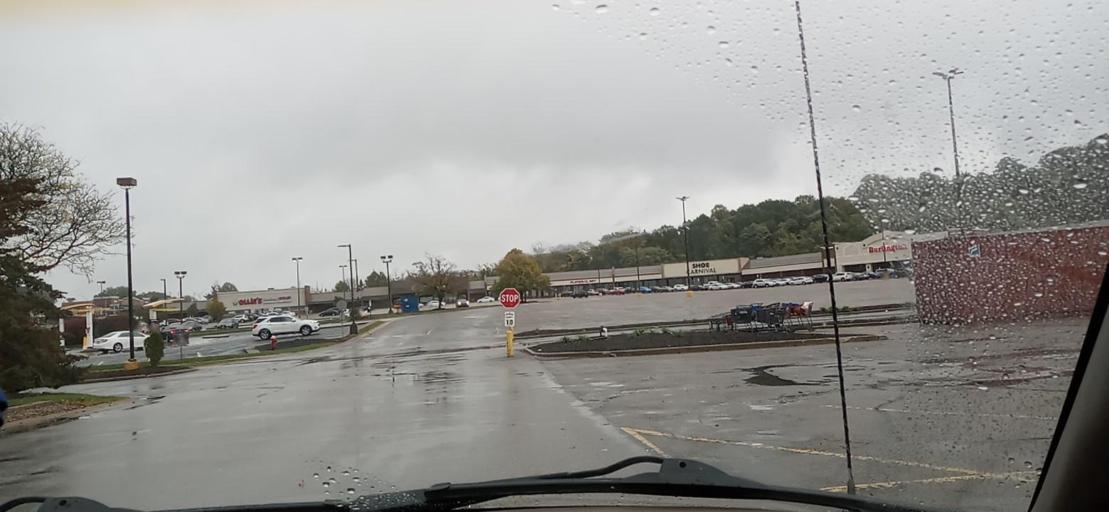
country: US
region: Ohio
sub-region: Summit County
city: Cuyahoga Falls
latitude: 41.1183
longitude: -81.4781
